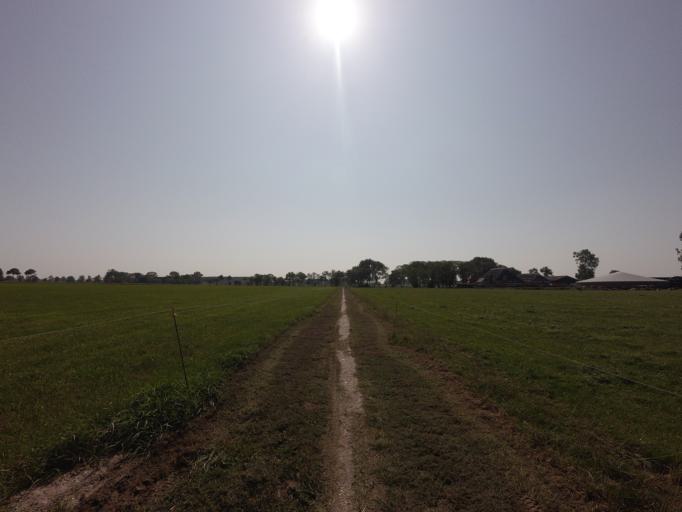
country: NL
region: Groningen
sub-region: Gemeente De Marne
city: Ulrum
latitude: 53.3511
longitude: 6.2983
